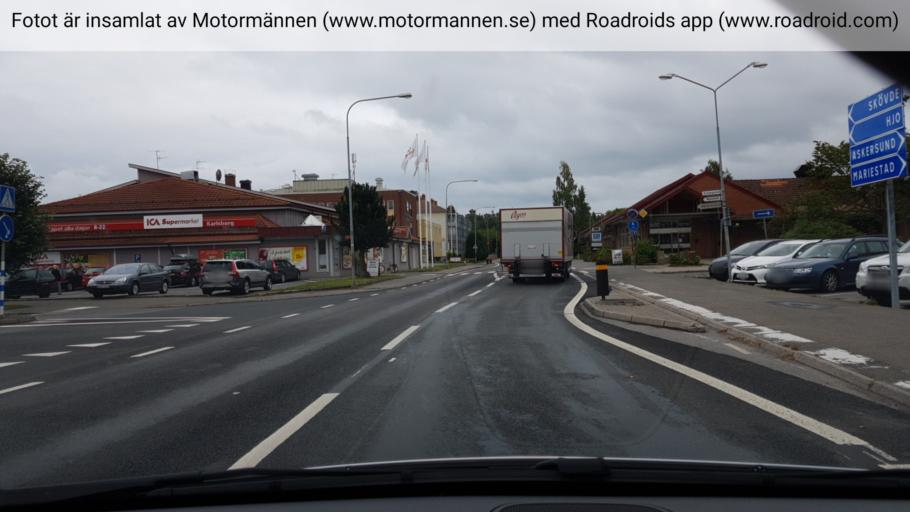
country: SE
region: Vaestra Goetaland
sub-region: Karlsborgs Kommun
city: Karlsborg
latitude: 58.5303
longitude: 14.5104
